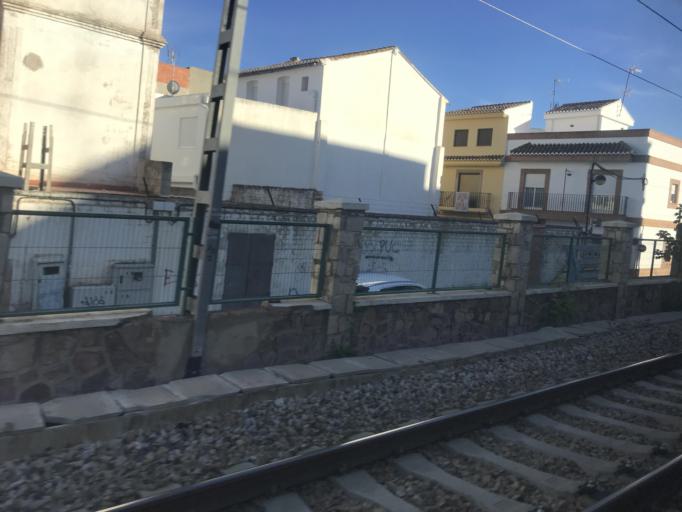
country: ES
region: Valencia
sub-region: Provincia de Valencia
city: Pucol
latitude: 39.6158
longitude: -0.3060
